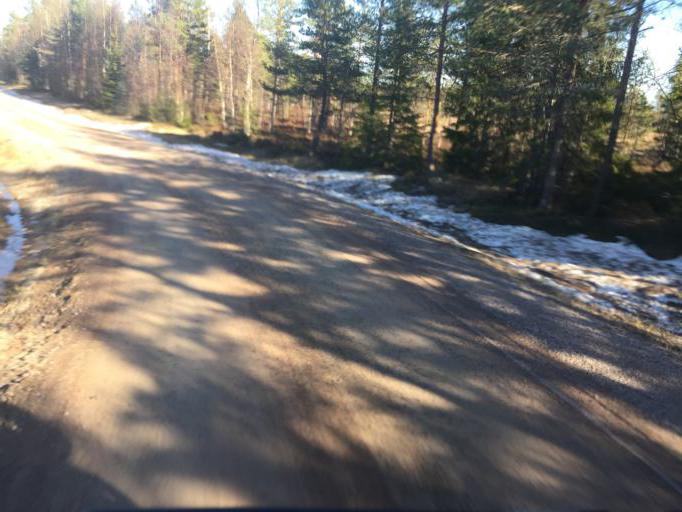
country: SE
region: Vaermland
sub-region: Filipstads Kommun
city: Lesjofors
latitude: 60.2487
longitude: 14.0890
